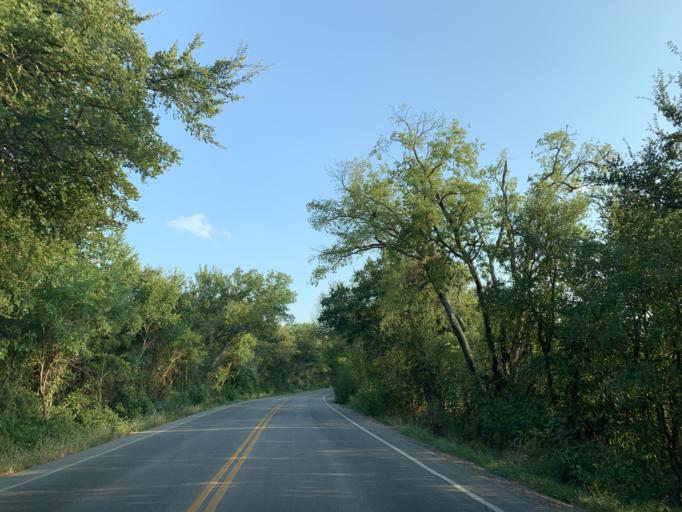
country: US
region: Texas
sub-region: Tarrant County
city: Hurst
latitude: 32.7845
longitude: -97.1778
